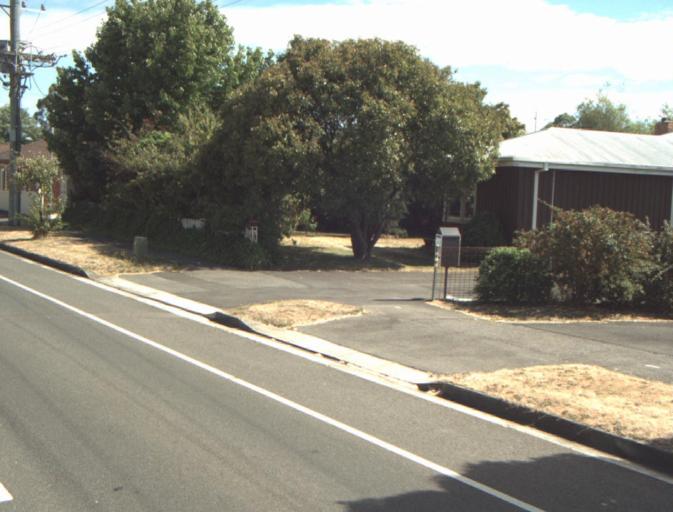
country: AU
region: Tasmania
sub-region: Launceston
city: Summerhill
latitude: -41.4637
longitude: 147.1347
